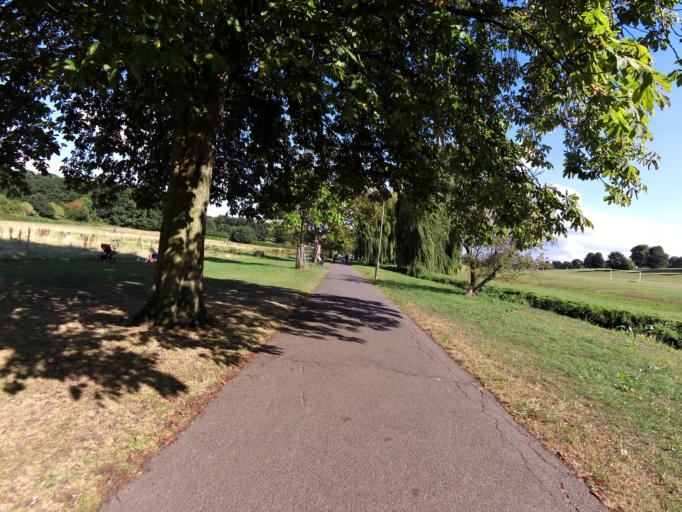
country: GB
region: England
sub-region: Greater London
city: Hadley Wood
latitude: 51.6385
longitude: -0.1566
